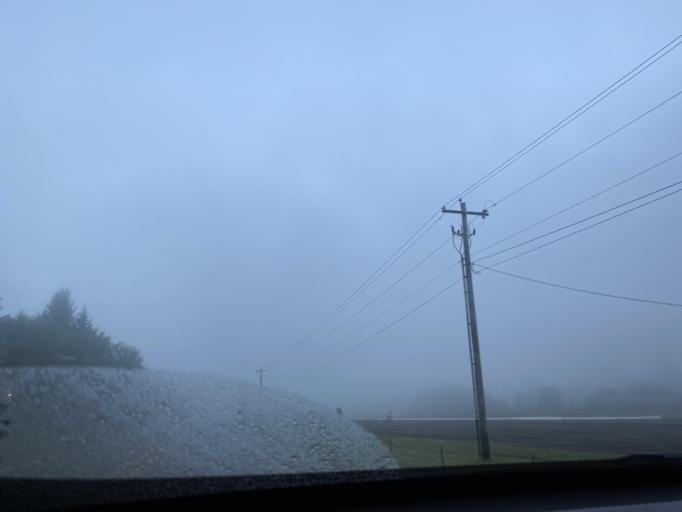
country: US
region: Washington
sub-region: Clallam County
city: Forks
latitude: 47.9370
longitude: -124.3942
